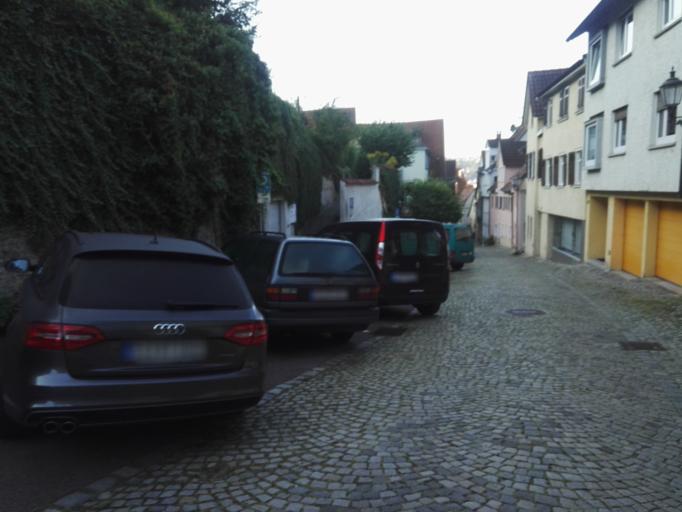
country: DE
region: Baden-Wuerttemberg
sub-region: Regierungsbezirk Stuttgart
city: Esslingen
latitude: 48.7454
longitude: 9.3073
